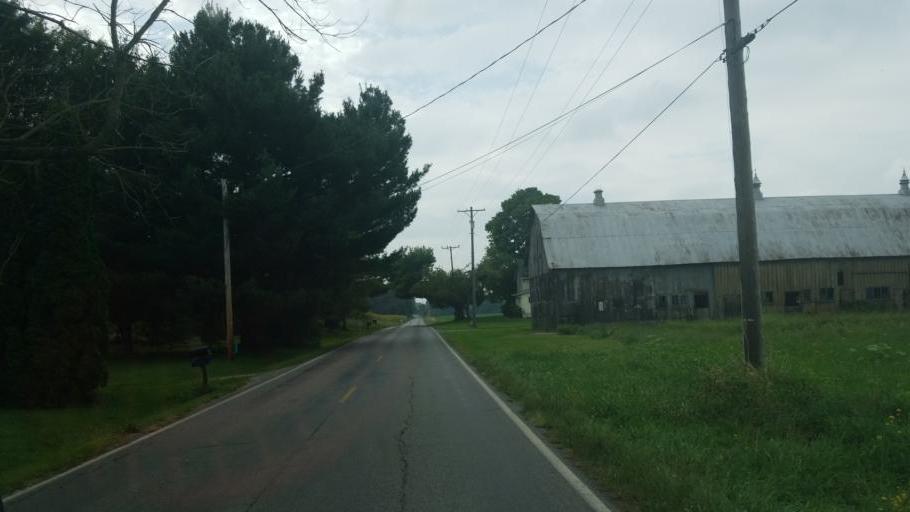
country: US
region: Ohio
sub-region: Wayne County
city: Creston
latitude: 40.9605
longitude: -81.8714
